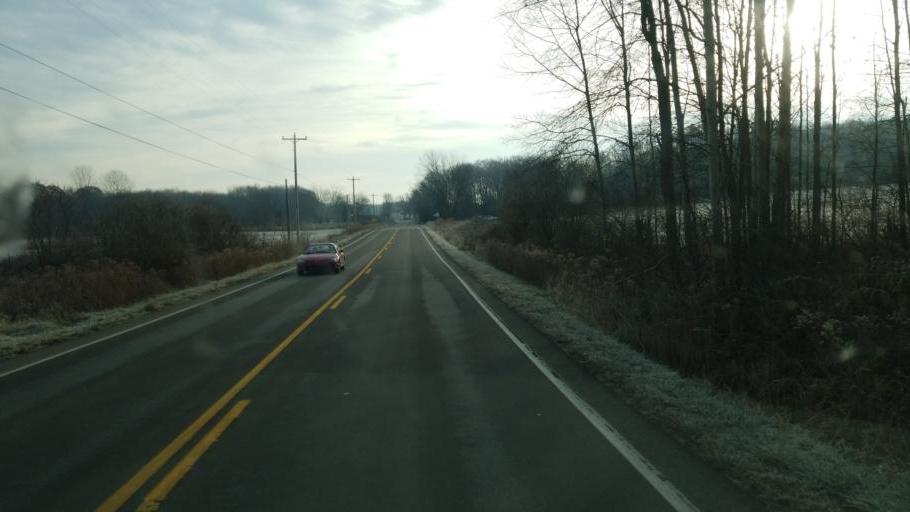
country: US
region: Pennsylvania
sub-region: Crawford County
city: Meadville
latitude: 41.5345
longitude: -80.1724
